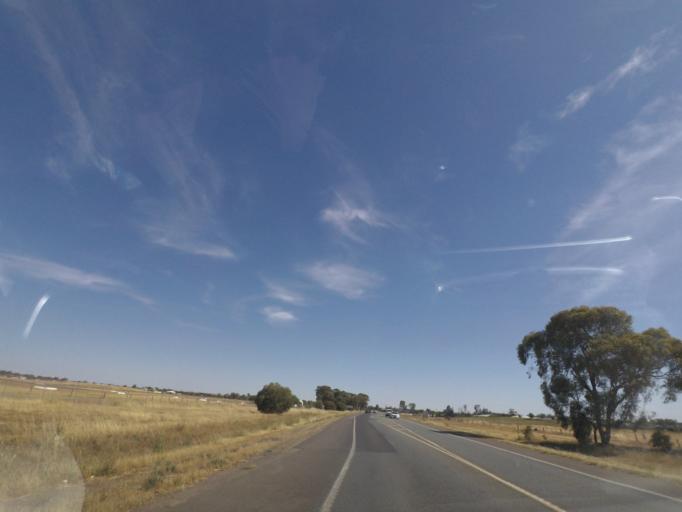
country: AU
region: Victoria
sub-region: Greater Shepparton
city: Shepparton
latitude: -36.4281
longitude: 145.3895
